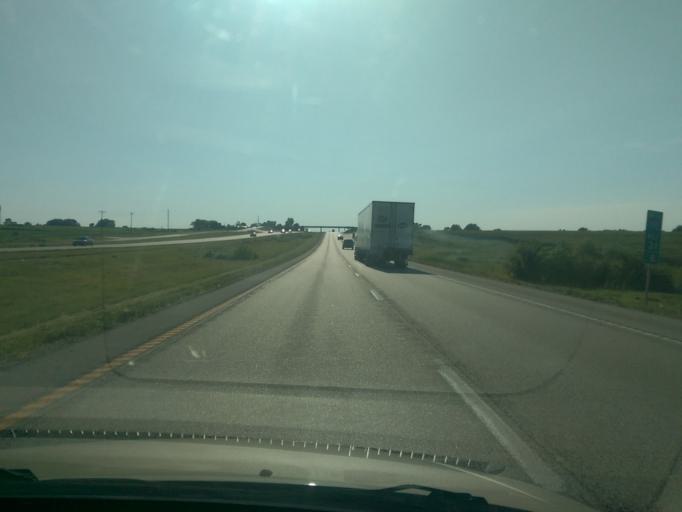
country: US
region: Missouri
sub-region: Jackson County
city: Oak Grove
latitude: 39.0114
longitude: -94.0617
